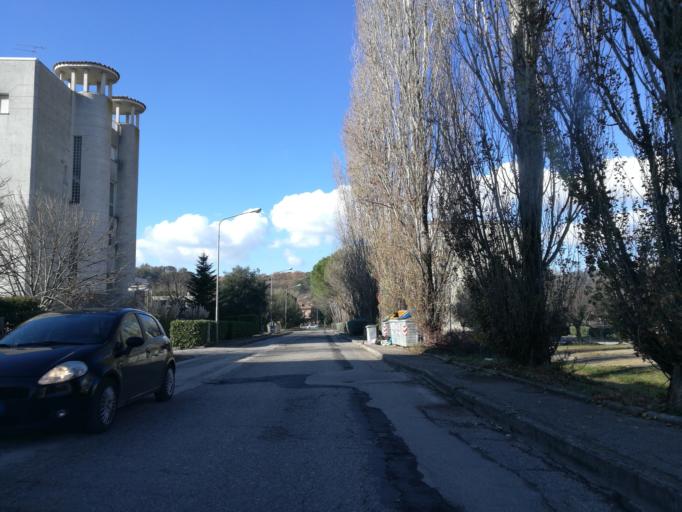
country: IT
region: Umbria
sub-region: Provincia di Perugia
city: Lacugnano
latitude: 43.0782
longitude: 12.3674
